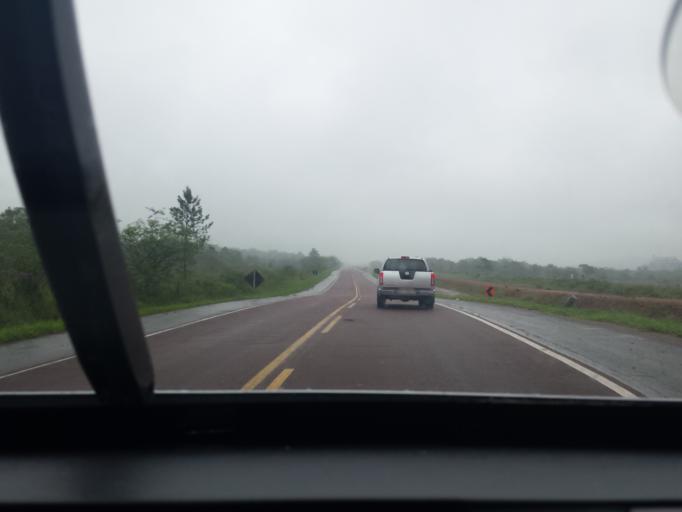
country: BR
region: Santa Catarina
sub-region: Itajai
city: Itajai
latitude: -26.8410
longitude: -48.7921
